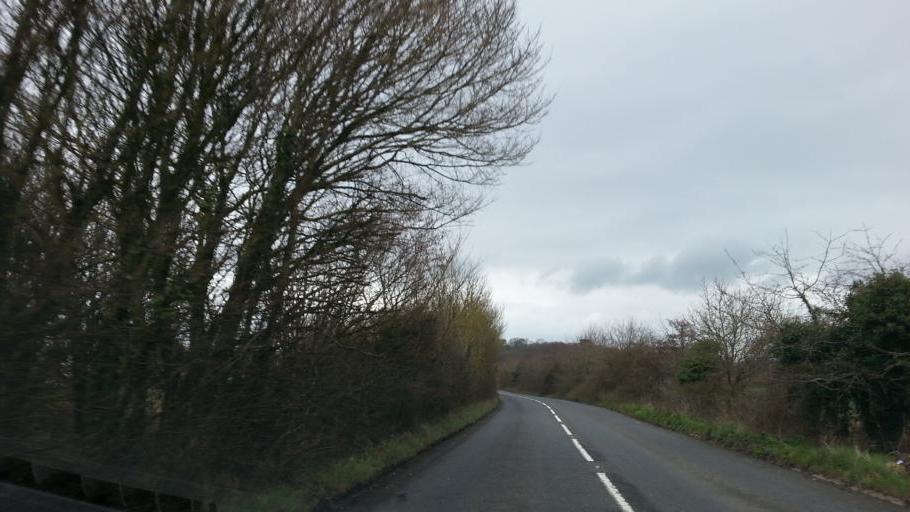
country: GB
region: England
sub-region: Devon
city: Appledore
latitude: 51.0358
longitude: -4.1920
